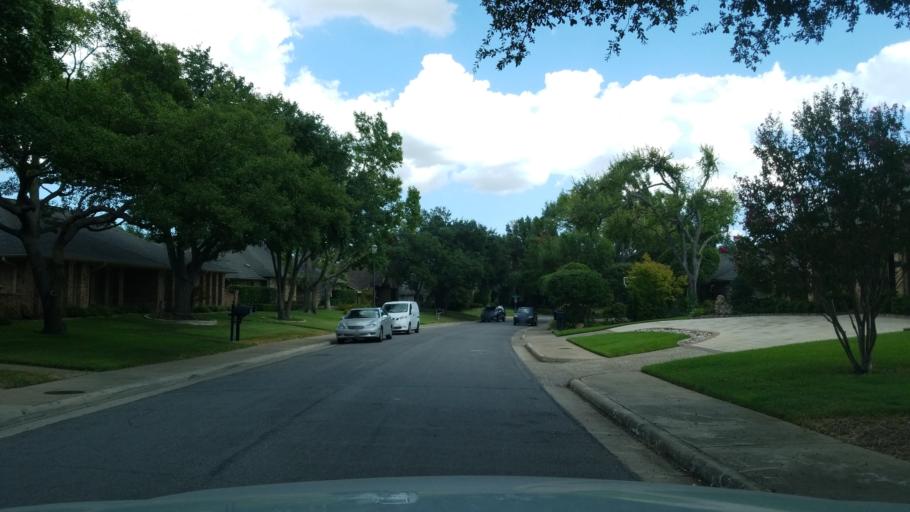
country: US
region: Texas
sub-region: Dallas County
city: Addison
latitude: 32.9655
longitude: -96.7984
